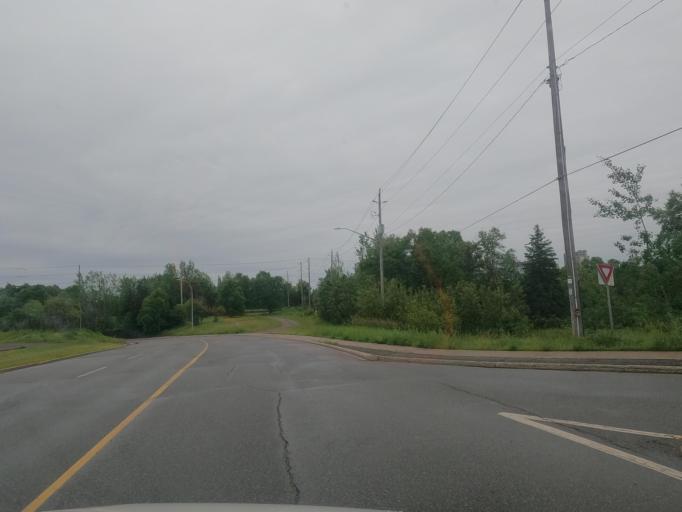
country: CA
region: Ontario
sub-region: Thunder Bay District
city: Thunder Bay
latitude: 48.4551
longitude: -89.1855
